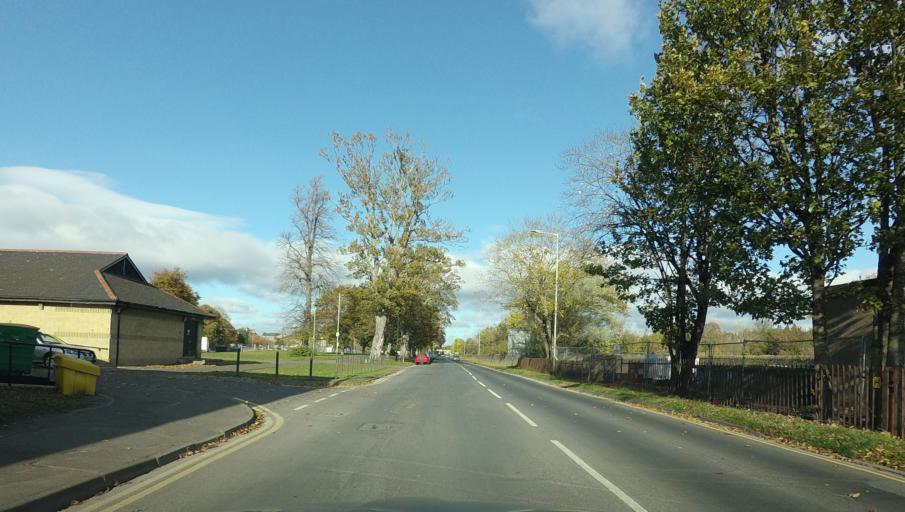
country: GB
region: Scotland
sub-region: Perth and Kinross
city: Perth
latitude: 56.3886
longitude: -3.4264
